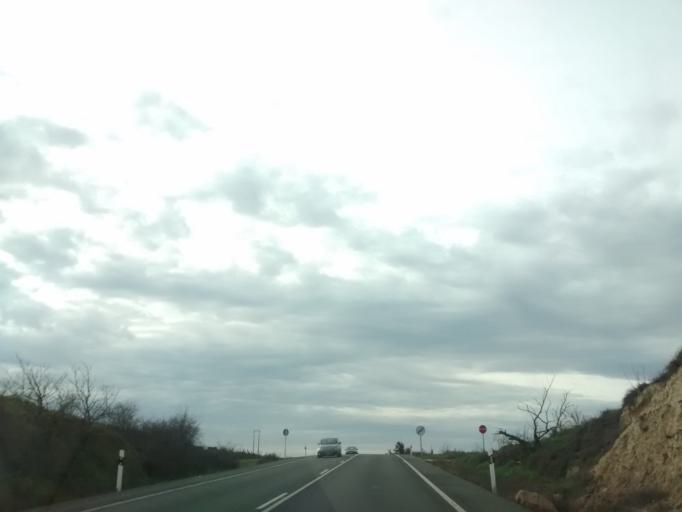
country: ES
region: La Rioja
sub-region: Provincia de La Rioja
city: San Asensio
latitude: 42.5107
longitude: -2.7230
